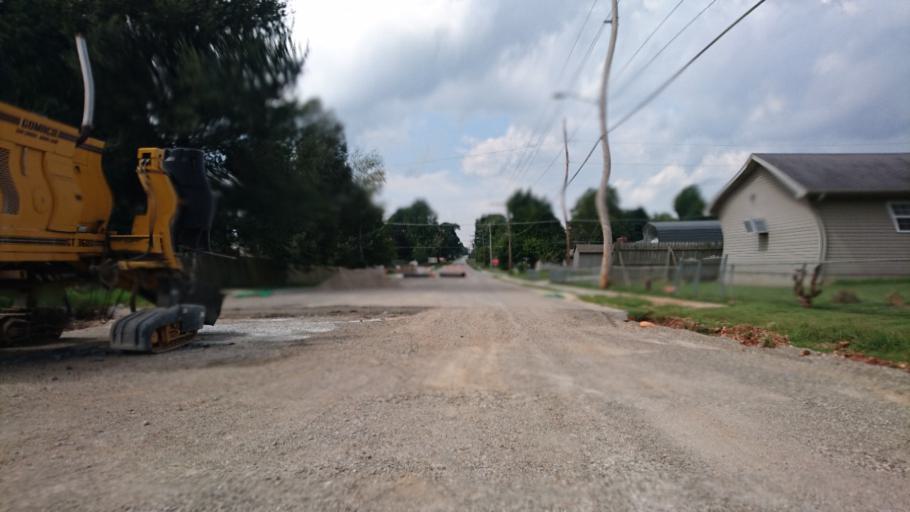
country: US
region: Missouri
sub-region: Greene County
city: Springfield
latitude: 37.2050
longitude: -93.3616
